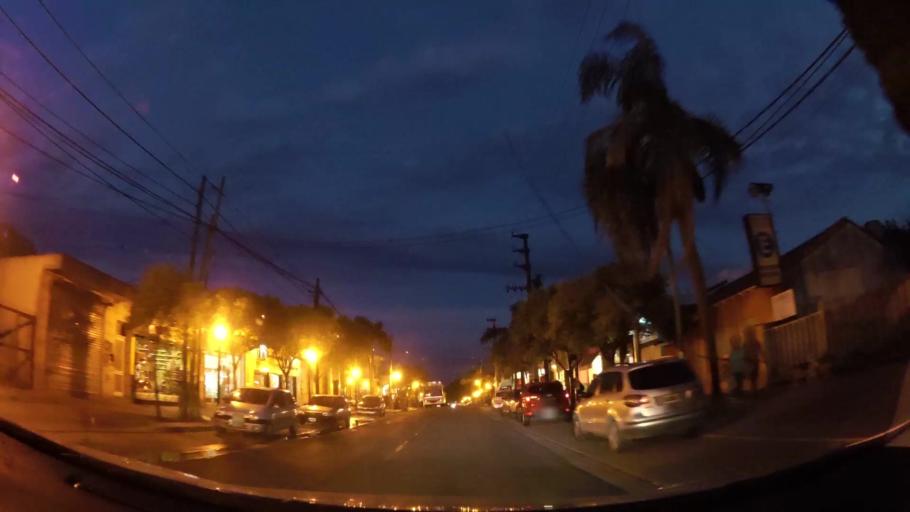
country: AR
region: Buenos Aires
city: Santa Catalina - Dique Lujan
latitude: -34.4109
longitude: -58.6874
